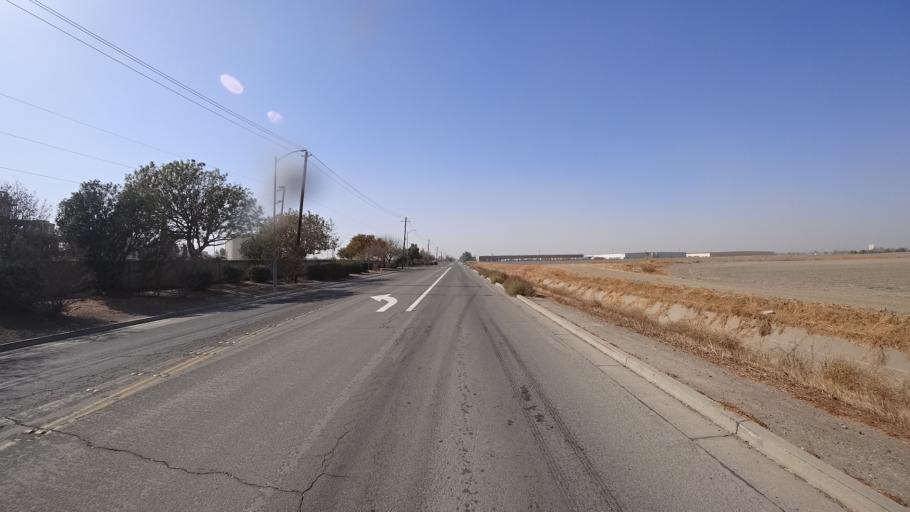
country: US
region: California
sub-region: Yolo County
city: Woodland
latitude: 38.6917
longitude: -121.7366
